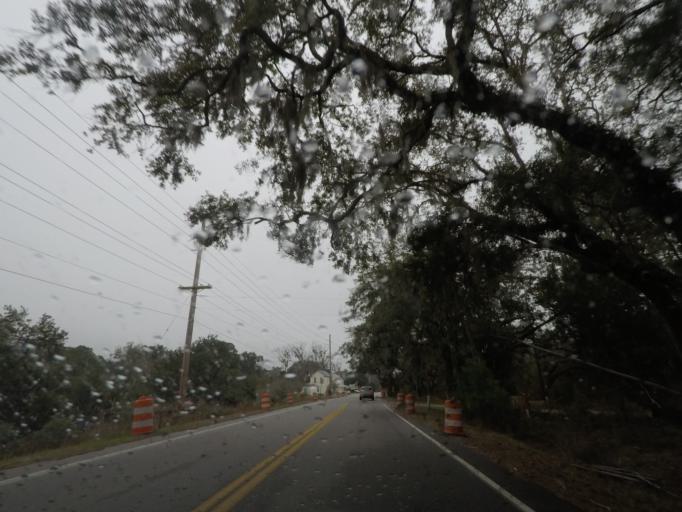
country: US
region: South Carolina
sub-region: Charleston County
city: Seabrook Island
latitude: 32.5613
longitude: -80.2802
